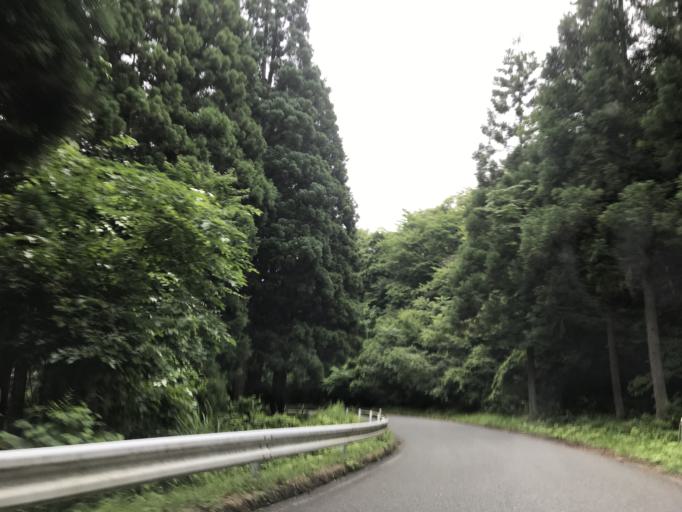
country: JP
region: Iwate
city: Ichinoseki
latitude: 38.8287
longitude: 141.2350
